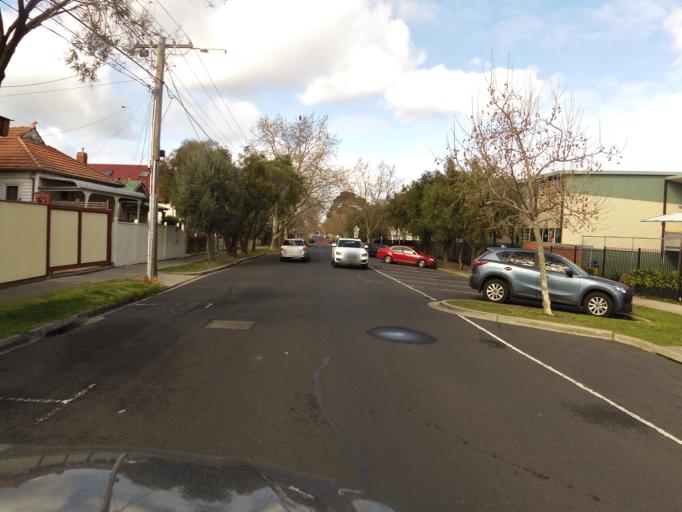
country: AU
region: Victoria
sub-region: Maribyrnong
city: Kingsville
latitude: -37.8148
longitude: 144.8855
